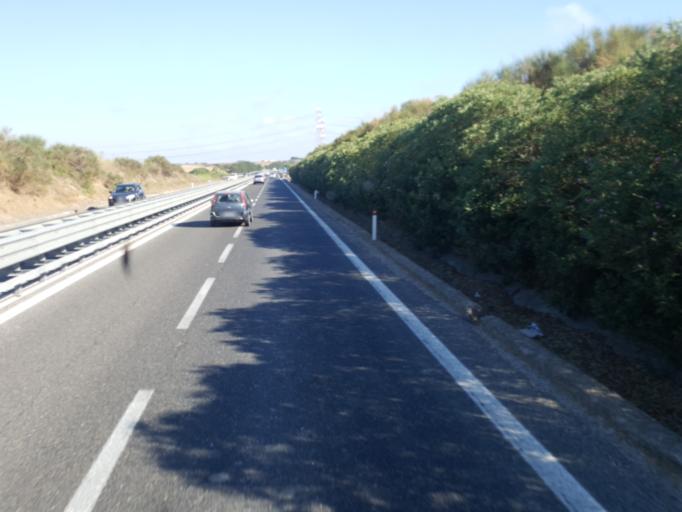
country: IT
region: Latium
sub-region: Provincia di Viterbo
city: Pescia Romana
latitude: 42.3796
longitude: 11.5532
